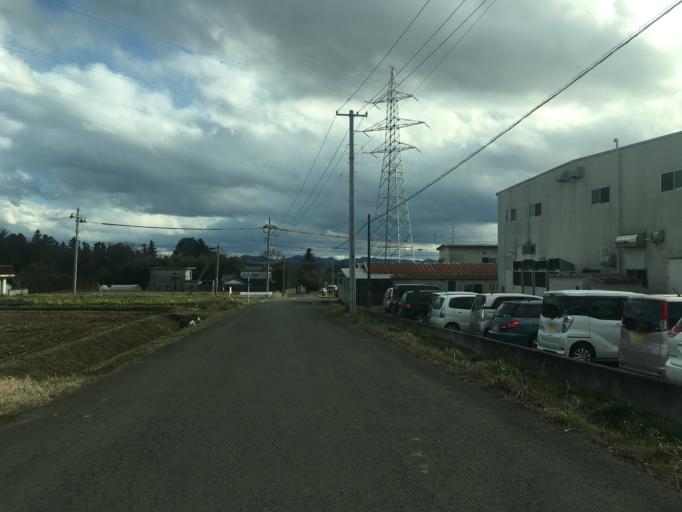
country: JP
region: Fukushima
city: Yanagawamachi-saiwaicho
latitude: 37.8878
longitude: 140.5767
